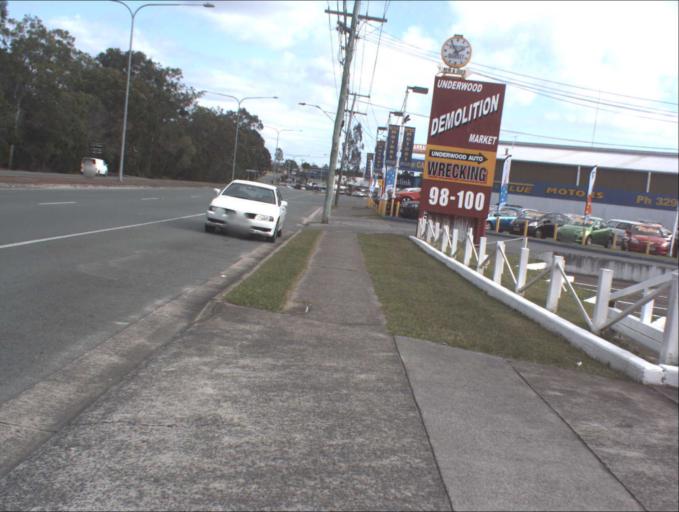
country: AU
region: Queensland
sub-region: Logan
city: Springwood
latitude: -27.6164
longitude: 153.1152
